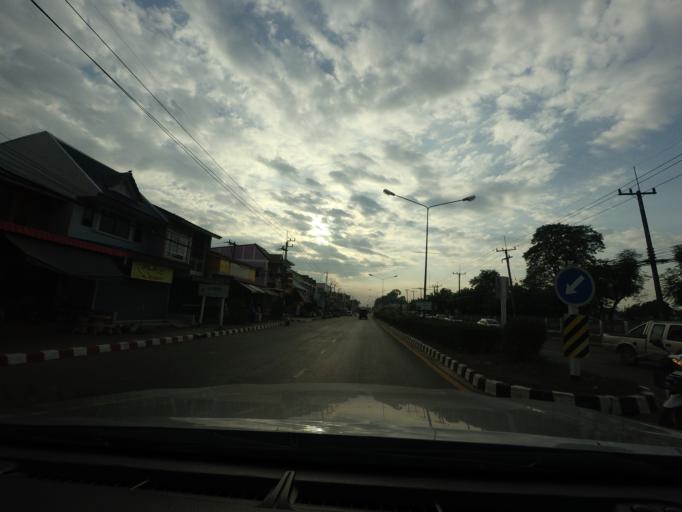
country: TH
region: Phitsanulok
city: Noen Maprang
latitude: 16.5675
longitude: 100.6366
